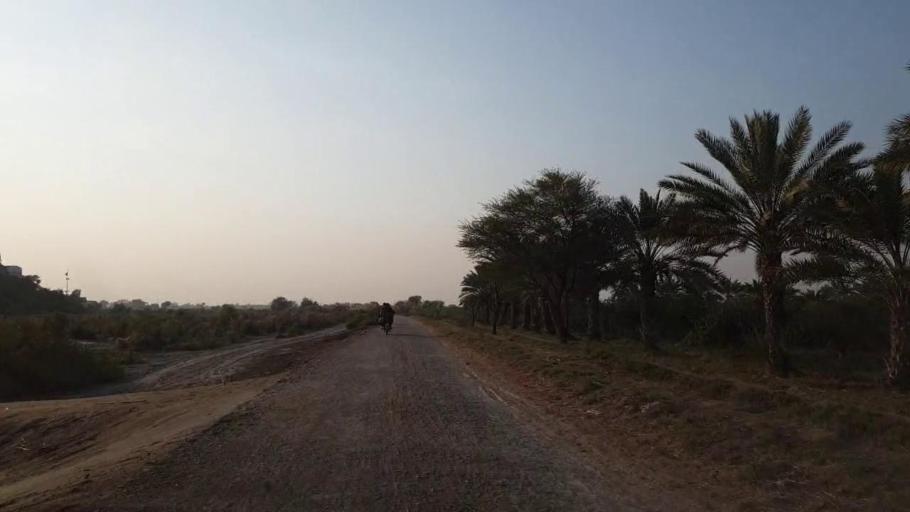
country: PK
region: Sindh
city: Pithoro
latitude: 25.6534
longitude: 69.2328
